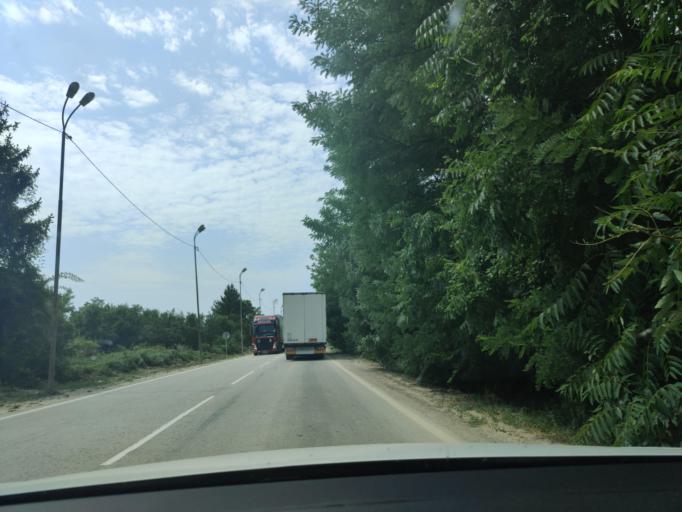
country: BG
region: Vidin
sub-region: Obshtina Dimovo
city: Dimovo
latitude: 43.7536
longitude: 22.7413
